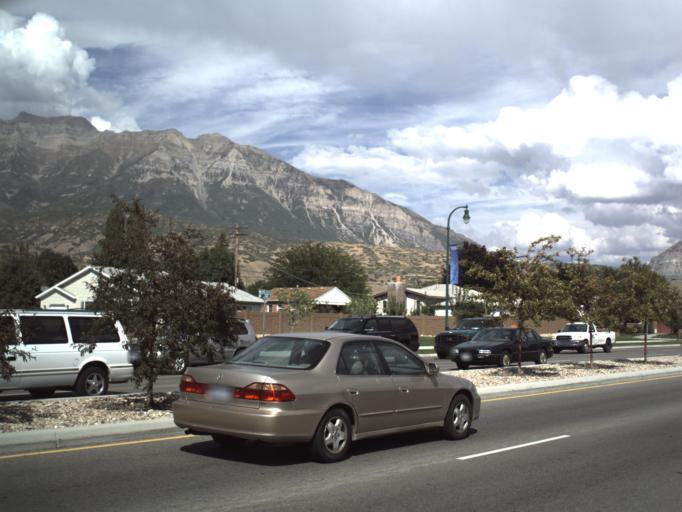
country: US
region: Utah
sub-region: Utah County
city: Orem
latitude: 40.3119
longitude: -111.6978
